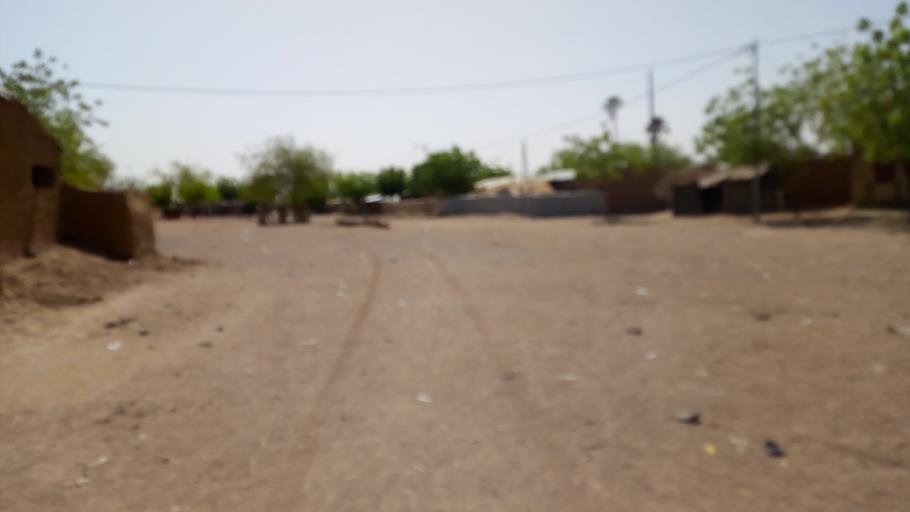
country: ML
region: Kayes
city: Yelimane
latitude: 14.6456
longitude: -10.7484
